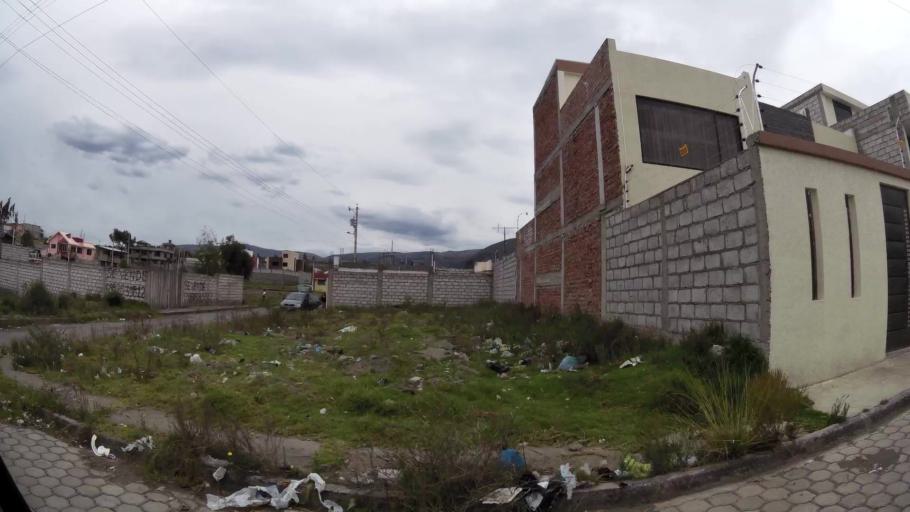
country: EC
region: Cotopaxi
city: Latacunga
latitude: -0.9586
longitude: -78.6080
